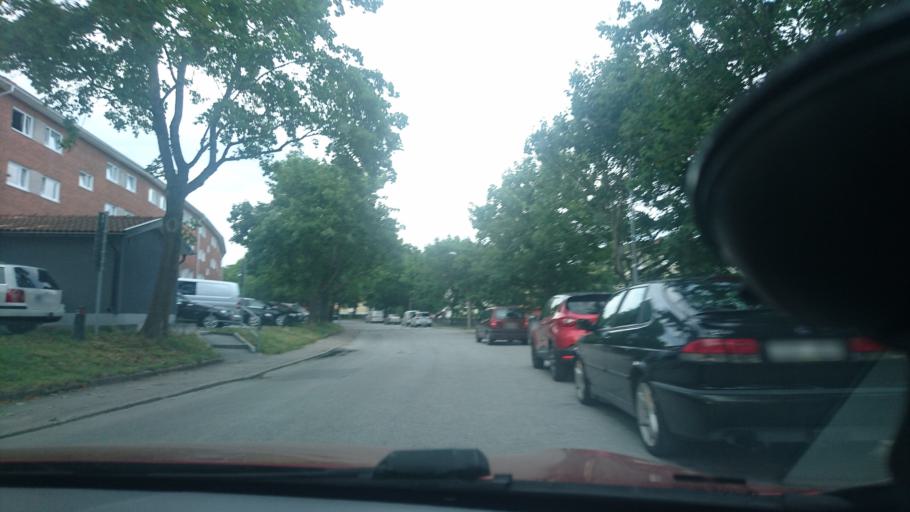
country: SE
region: Stockholm
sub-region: Upplands Vasby Kommun
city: Upplands Vaesby
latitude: 59.5214
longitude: 17.8950
